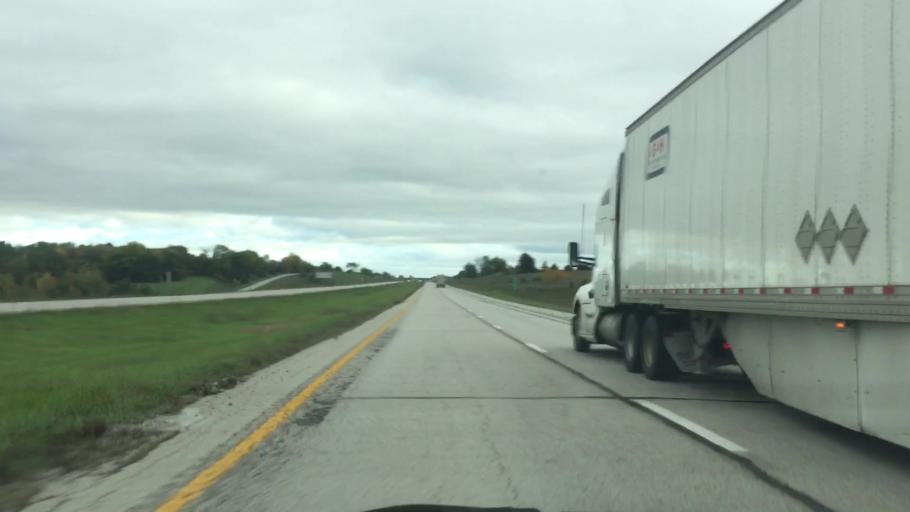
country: US
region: Missouri
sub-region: Harrison County
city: Bethany
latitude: 40.1420
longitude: -94.0425
